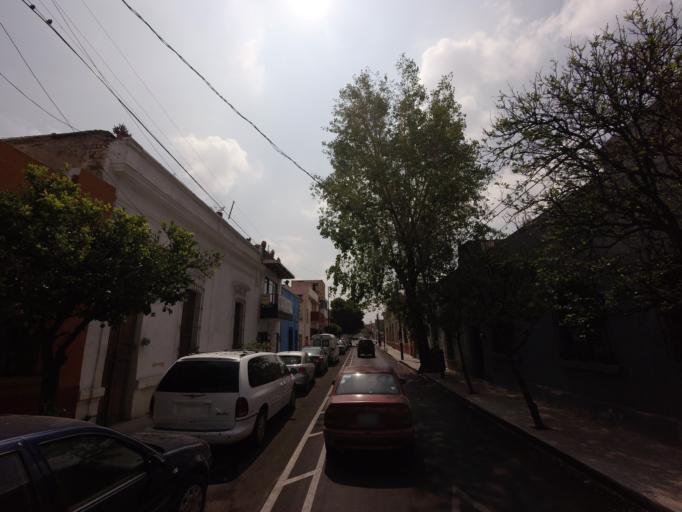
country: MX
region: Jalisco
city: Guadalajara
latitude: 20.6787
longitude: -103.3552
